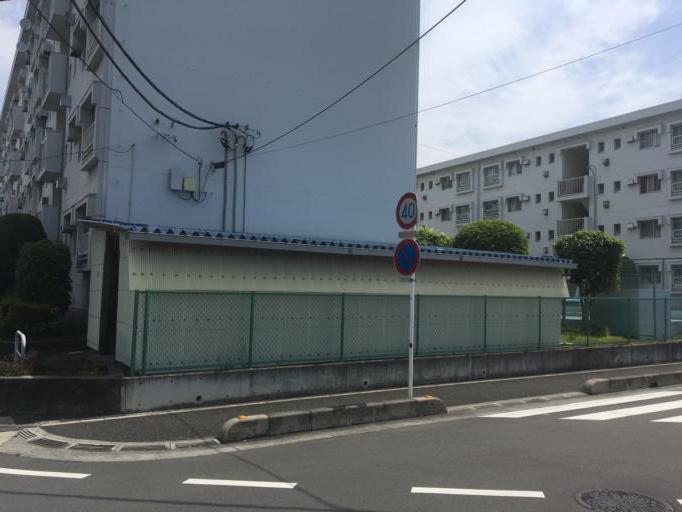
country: JP
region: Saitama
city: Shimotoda
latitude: 35.8419
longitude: 139.6513
